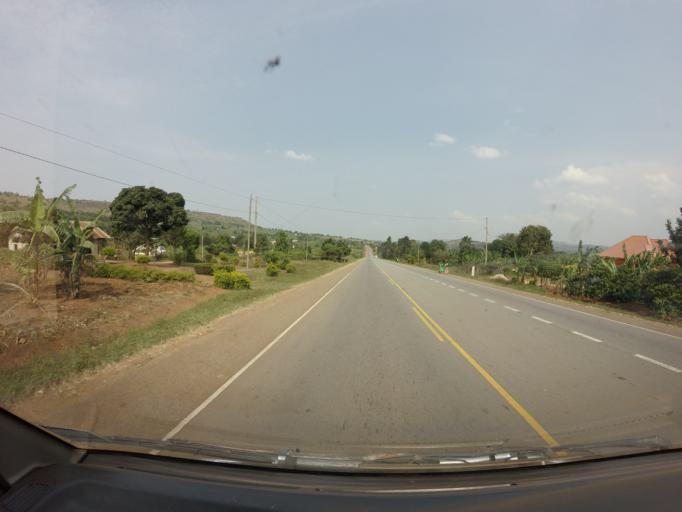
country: UG
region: Central Region
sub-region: Lwengo District
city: Lwengo
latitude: -0.3962
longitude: 31.3529
